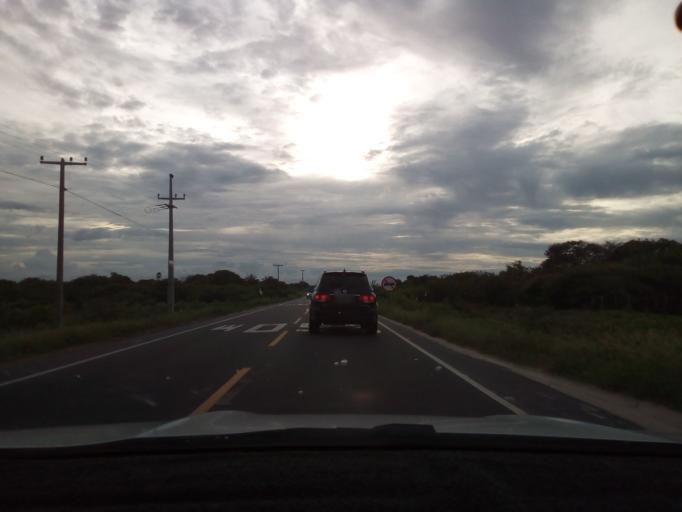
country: BR
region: Ceara
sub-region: Aracati
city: Aracati
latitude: -4.3945
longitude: -37.8648
